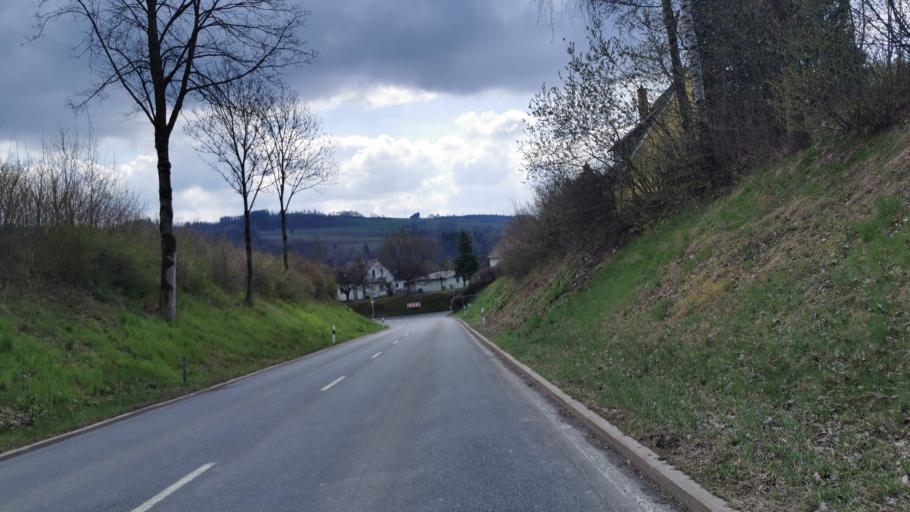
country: DE
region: Bavaria
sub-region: Upper Franconia
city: Pressig
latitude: 50.3634
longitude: 11.3144
